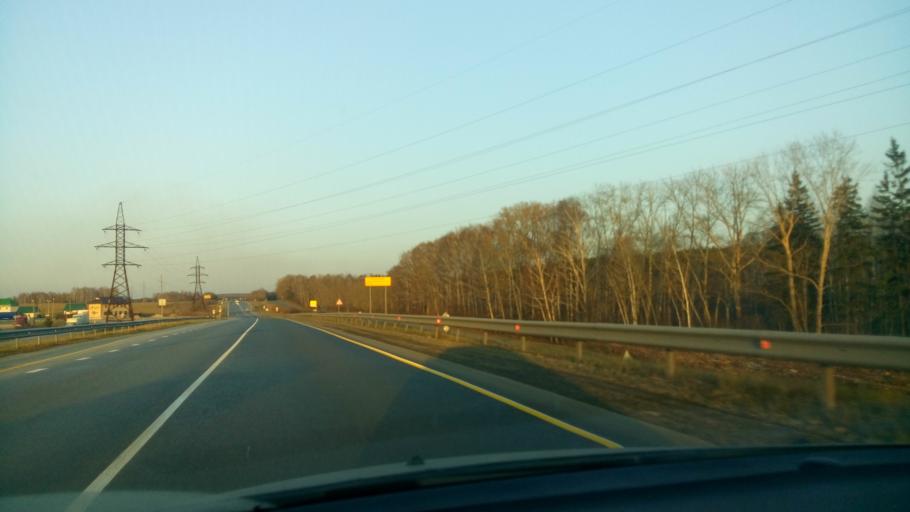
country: RU
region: Sverdlovsk
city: Obukhovskoye
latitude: 56.8411
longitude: 62.5851
